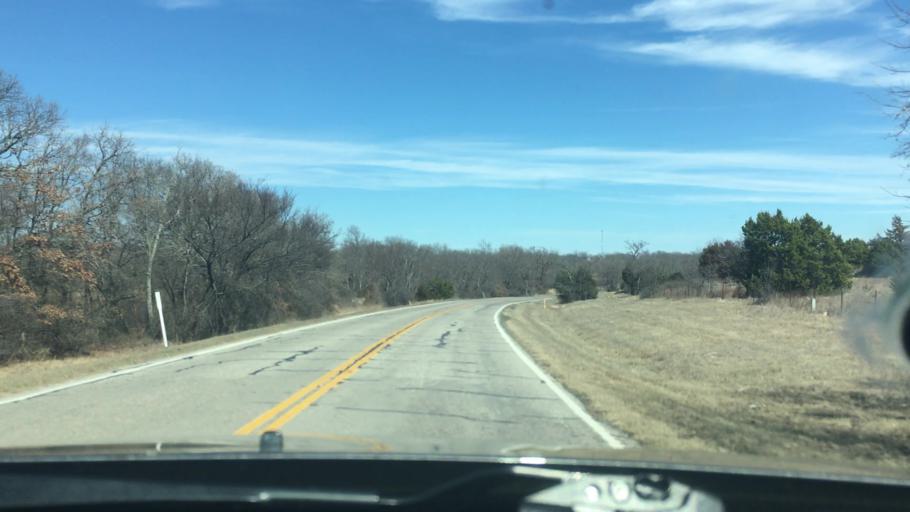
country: US
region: Oklahoma
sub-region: Carter County
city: Dickson
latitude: 34.3212
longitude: -96.9602
